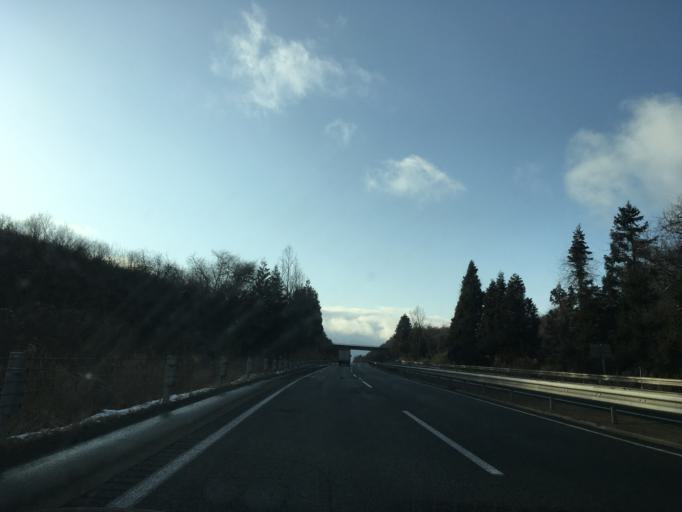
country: JP
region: Miyagi
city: Okawara
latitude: 38.1587
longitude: 140.6728
